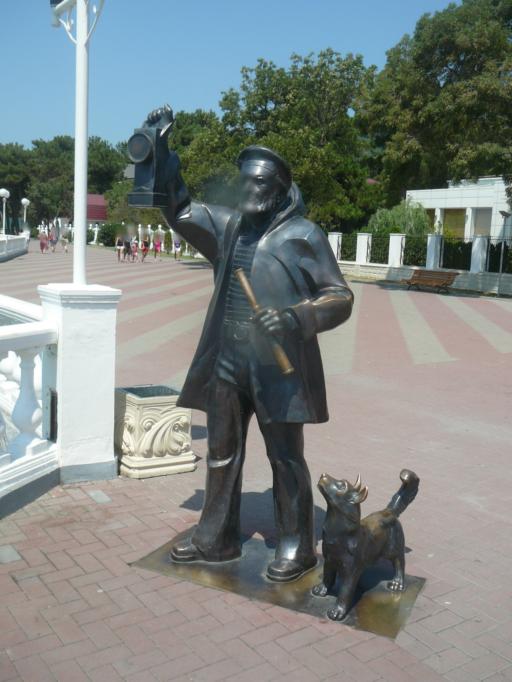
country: RU
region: Krasnodarskiy
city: Gelendzhik
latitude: 44.5738
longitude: 38.0681
